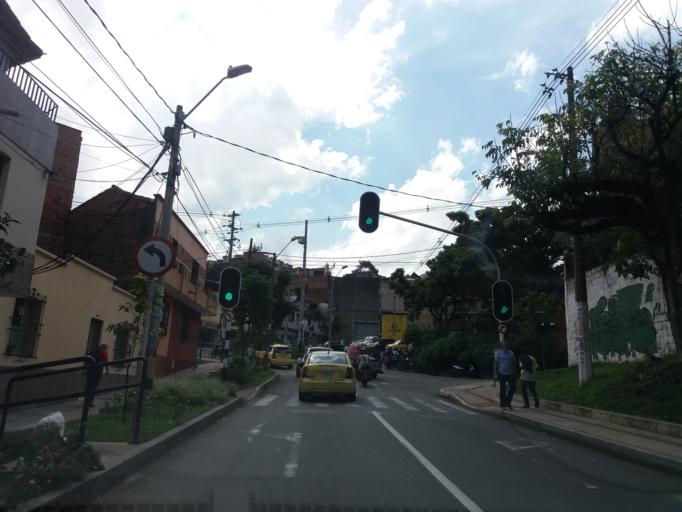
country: CO
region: Antioquia
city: Medellin
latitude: 6.2838
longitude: -75.5620
